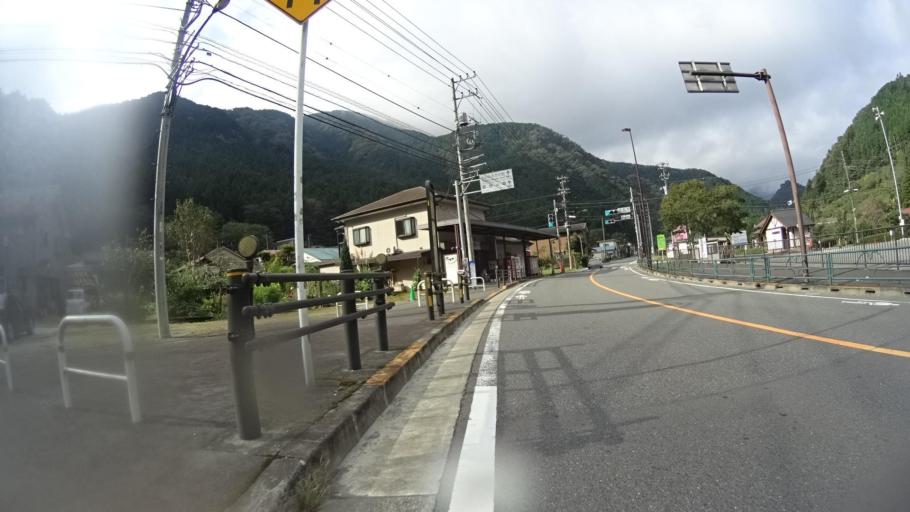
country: JP
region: Tokyo
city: Itsukaichi
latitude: 35.7246
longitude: 139.1812
